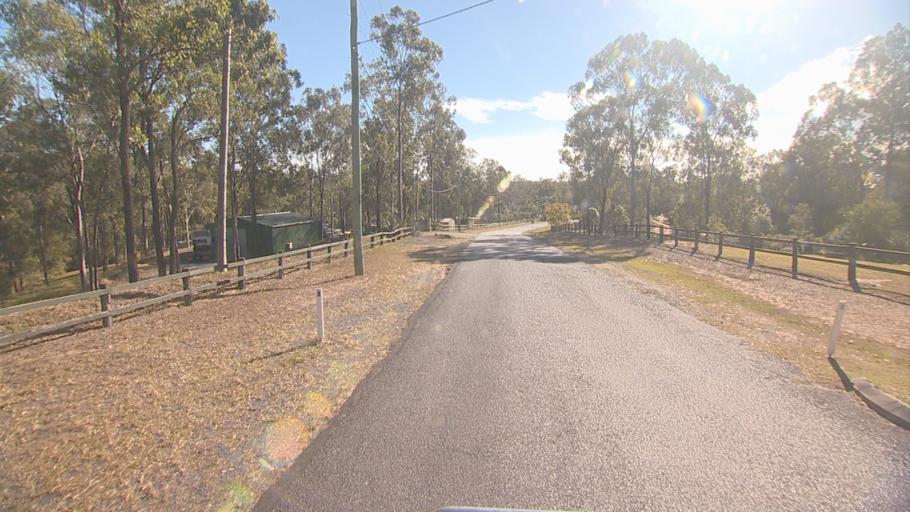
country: AU
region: Queensland
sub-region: Ipswich
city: Springfield Lakes
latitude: -27.7004
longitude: 152.9298
